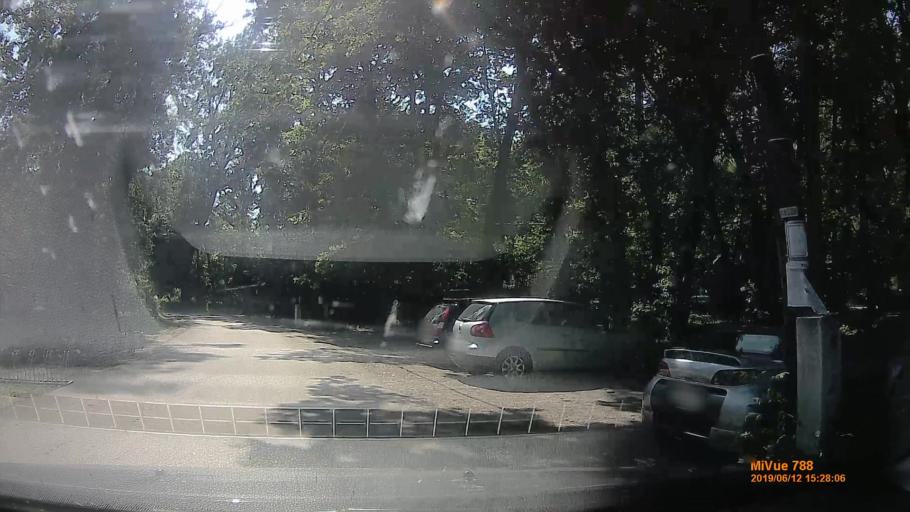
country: HU
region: Csongrad
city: Mako
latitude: 46.1980
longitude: 20.4732
